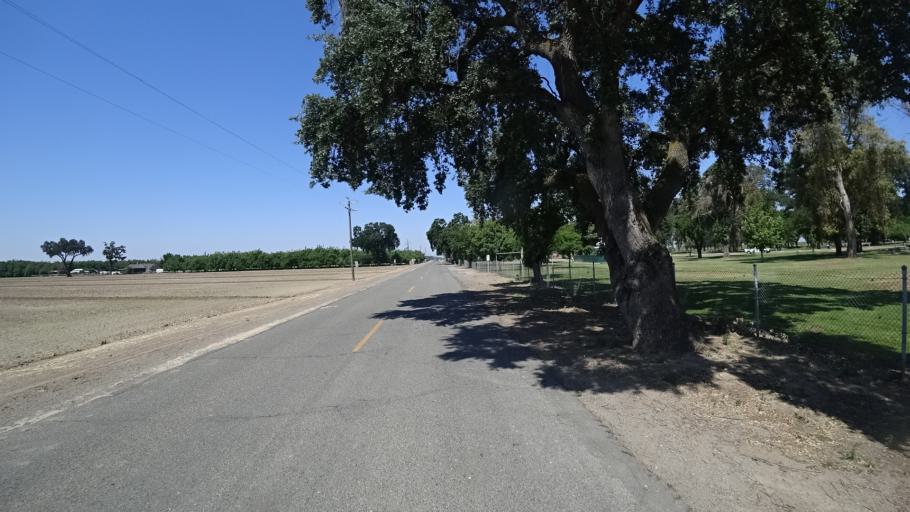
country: US
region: California
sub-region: Kings County
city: Lemoore
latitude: 36.3718
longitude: -119.7595
